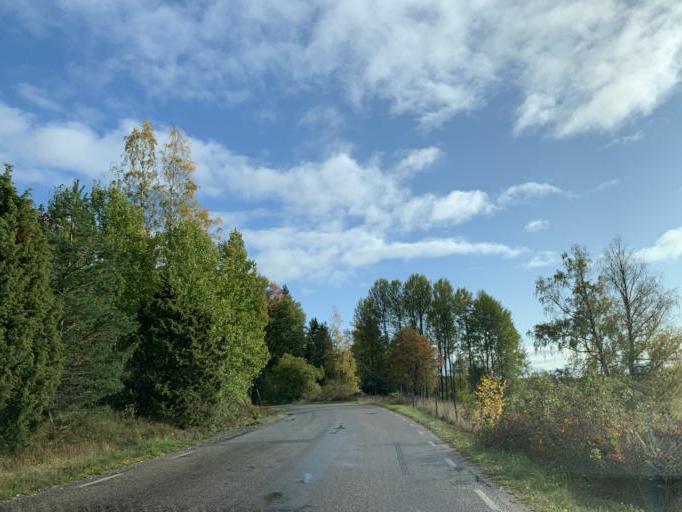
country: SE
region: Soedermanland
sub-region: Eskilstuna Kommun
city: Kvicksund
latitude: 59.3208
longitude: 16.2670
